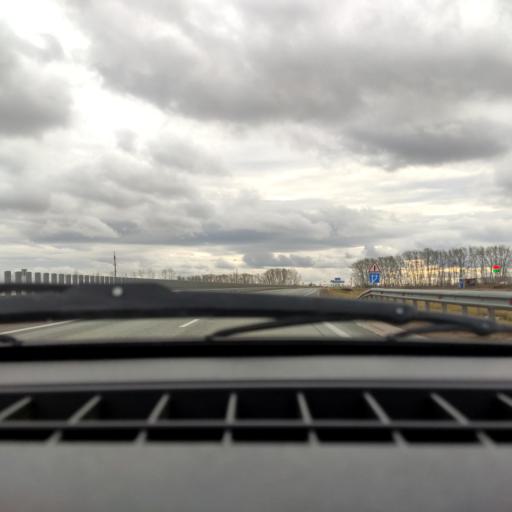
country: RU
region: Bashkortostan
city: Asanovo
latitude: 54.9637
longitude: 55.5836
